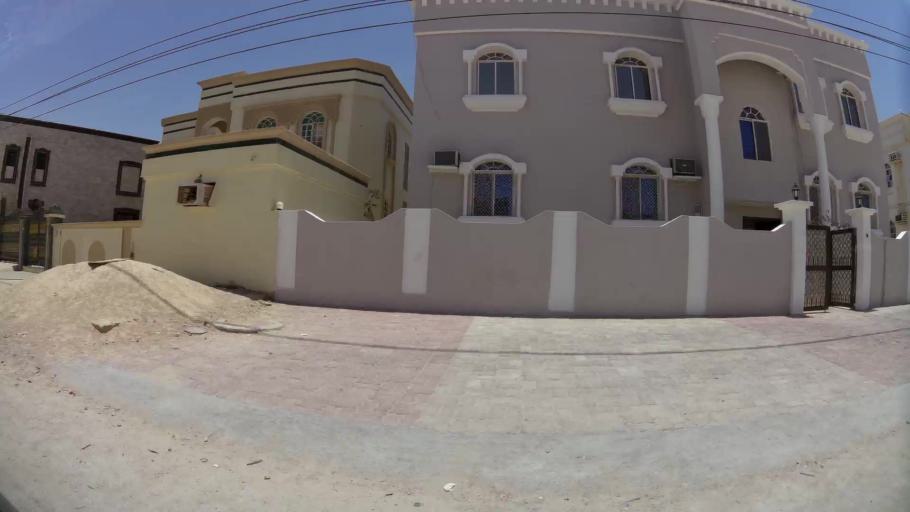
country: OM
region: Zufar
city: Salalah
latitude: 17.0821
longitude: 54.1598
